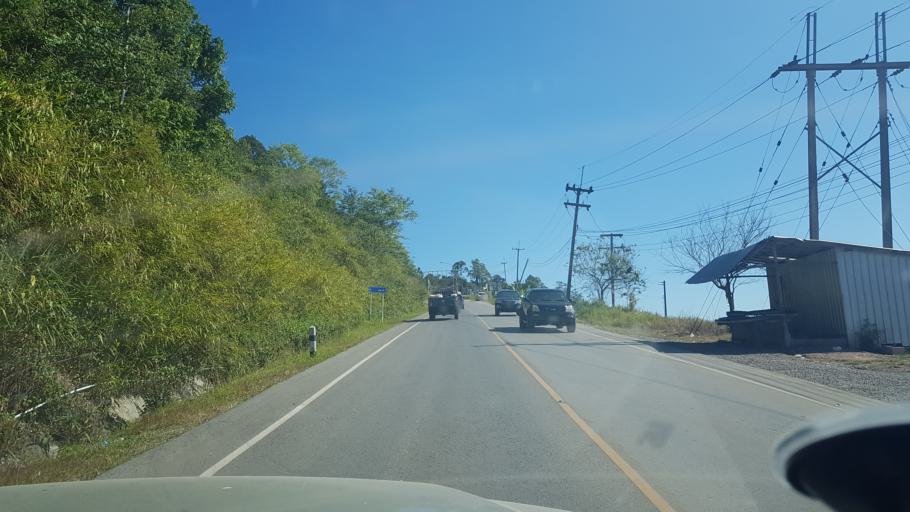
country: TH
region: Phetchabun
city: Lom Kao
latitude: 16.8915
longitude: 101.0968
